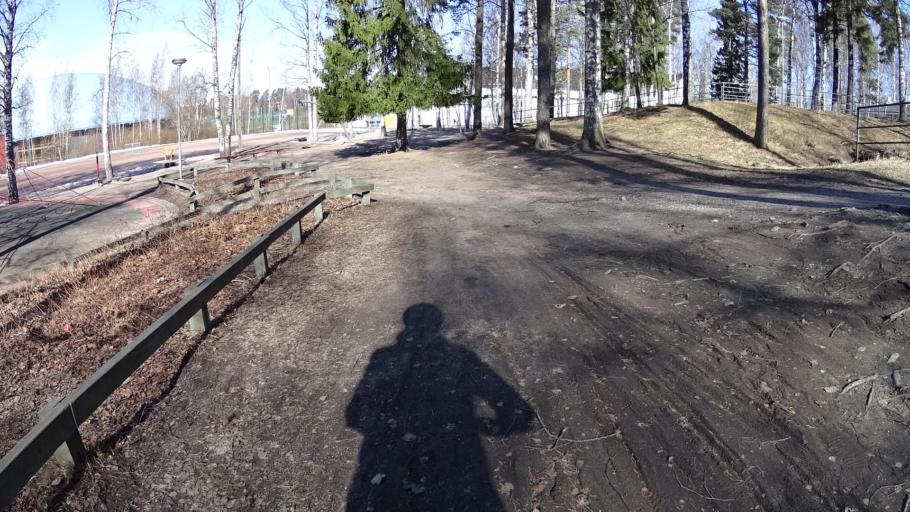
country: FI
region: Uusimaa
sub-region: Helsinki
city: Koukkuniemi
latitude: 60.1758
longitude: 24.7867
